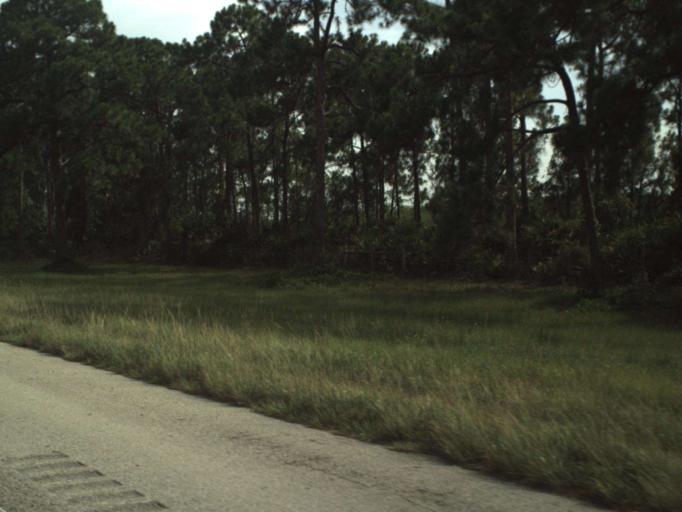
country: US
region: Florida
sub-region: Saint Lucie County
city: Port Saint Lucie
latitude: 27.2218
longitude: -80.4016
